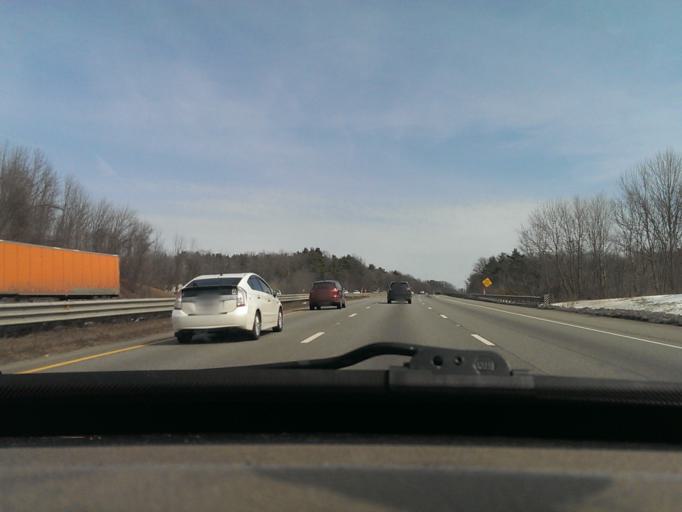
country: US
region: Massachusetts
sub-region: Worcester County
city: Charlton
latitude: 42.1522
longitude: -71.9876
